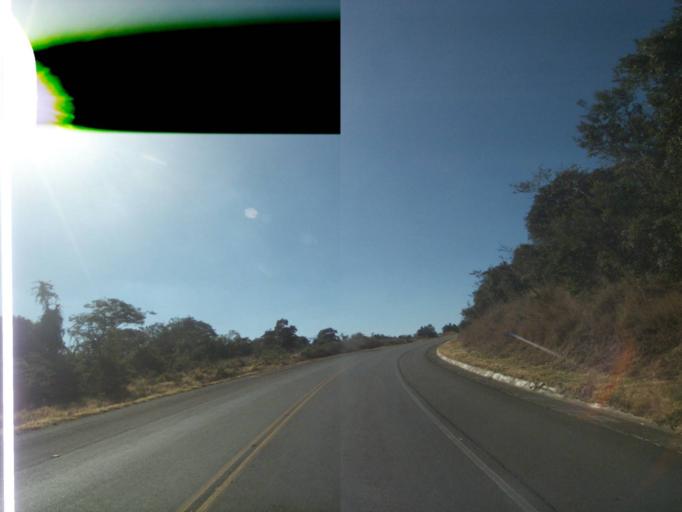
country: BR
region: Parana
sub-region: Tibagi
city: Tibagi
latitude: -24.7869
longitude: -50.4703
